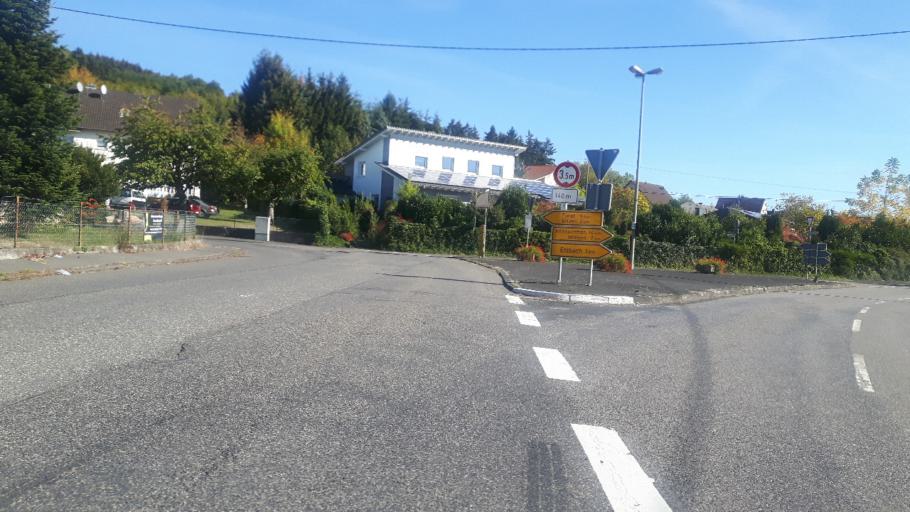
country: DE
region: Rheinland-Pfalz
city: Etzbach
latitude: 50.7806
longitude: 7.6784
